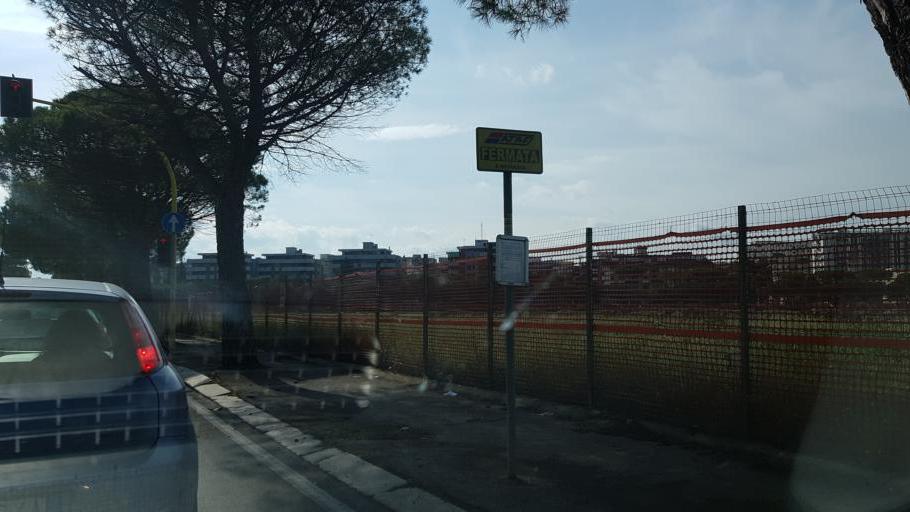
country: IT
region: Apulia
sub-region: Provincia di Foggia
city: Foggia
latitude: 41.4576
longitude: 15.5643
